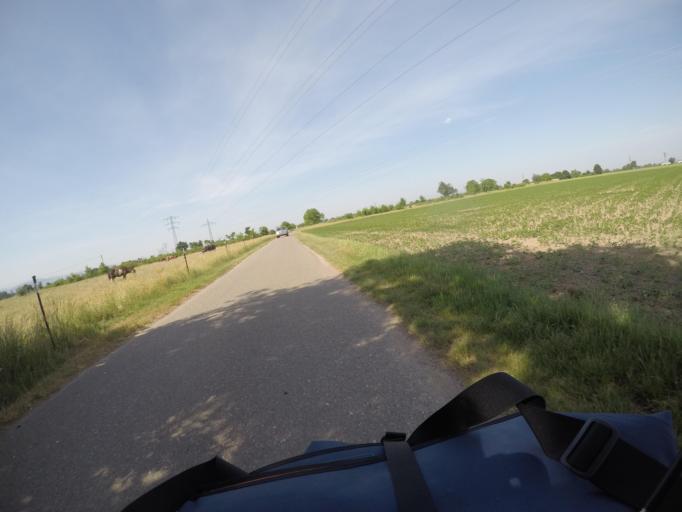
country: DE
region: Baden-Wuerttemberg
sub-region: Karlsruhe Region
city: Bietigheim
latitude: 48.9019
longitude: 8.2733
